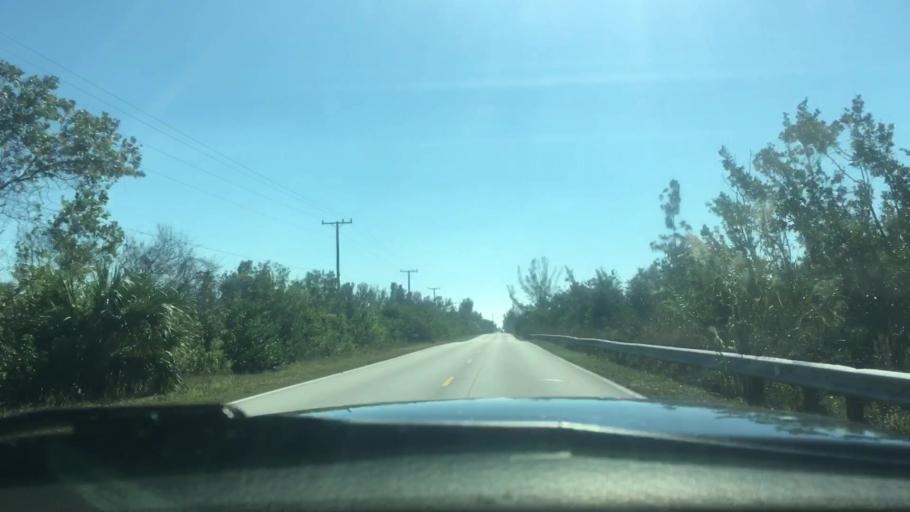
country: US
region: Florida
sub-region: Miami-Dade County
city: Florida City
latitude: 25.3704
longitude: -80.4321
